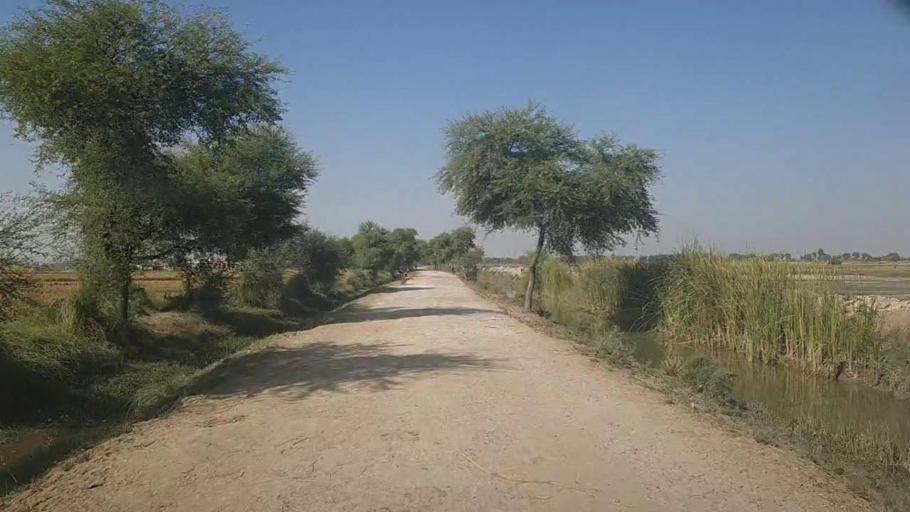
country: PK
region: Sindh
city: Thul
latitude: 28.3085
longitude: 68.7694
